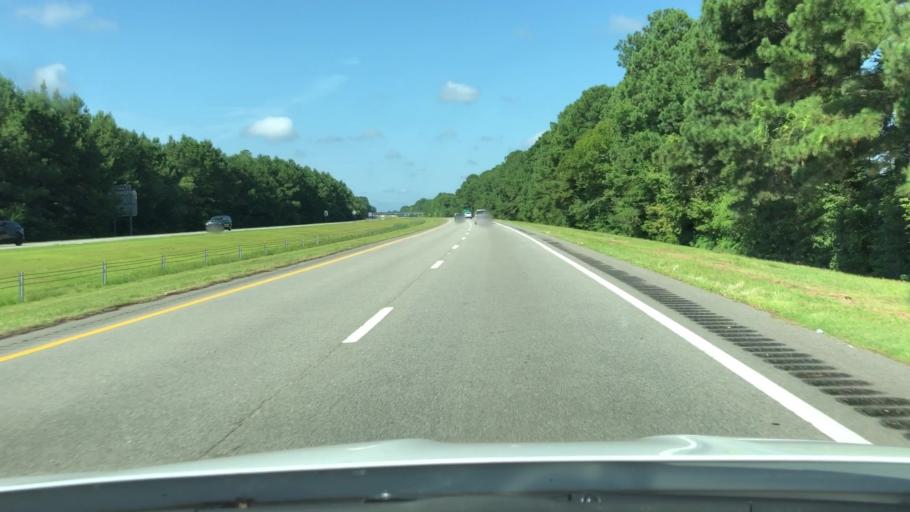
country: US
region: North Carolina
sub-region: Chowan County
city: Edenton
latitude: 36.0878
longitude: -76.5886
